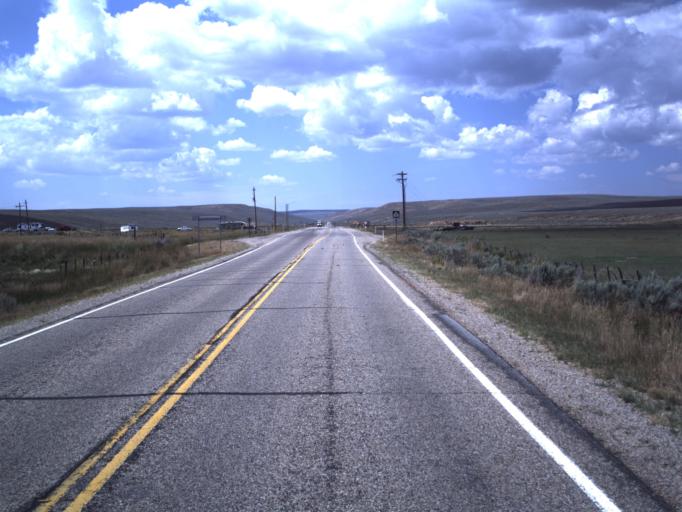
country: US
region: Utah
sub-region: Rich County
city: Randolph
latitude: 41.7730
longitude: -111.1175
